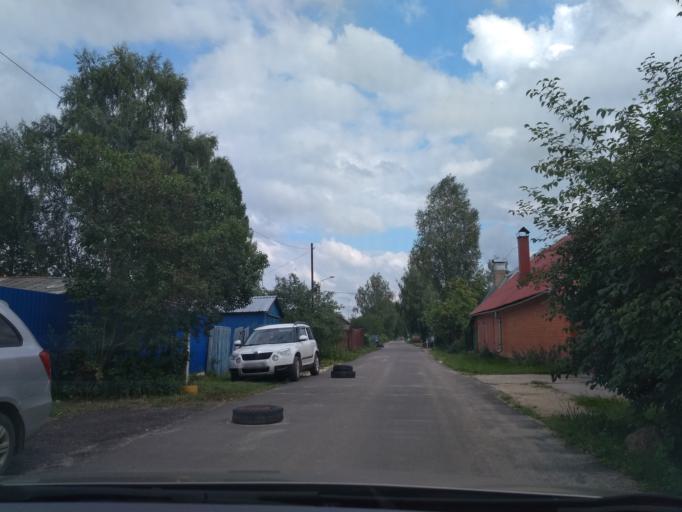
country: RU
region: Moskovskaya
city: Kabanovo
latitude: 55.7849
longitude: 38.9223
